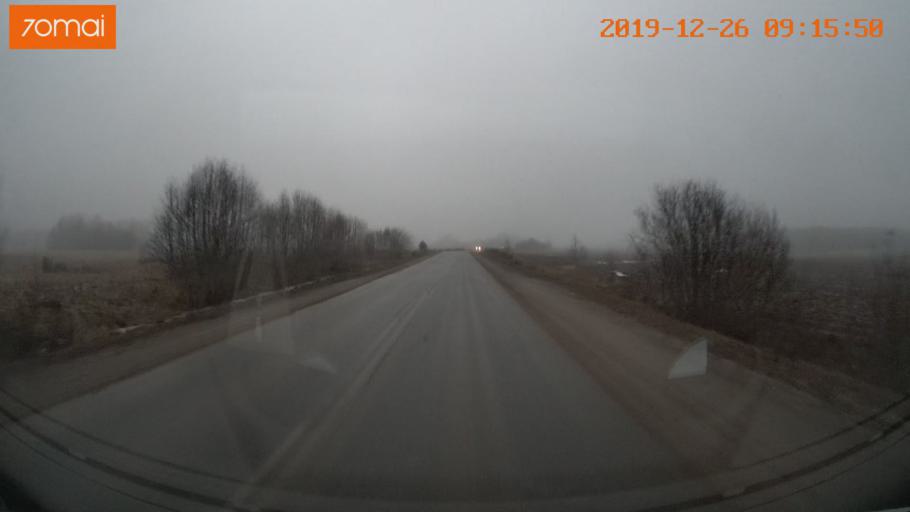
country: RU
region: Vologda
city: Gryazovets
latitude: 58.9101
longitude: 40.2393
